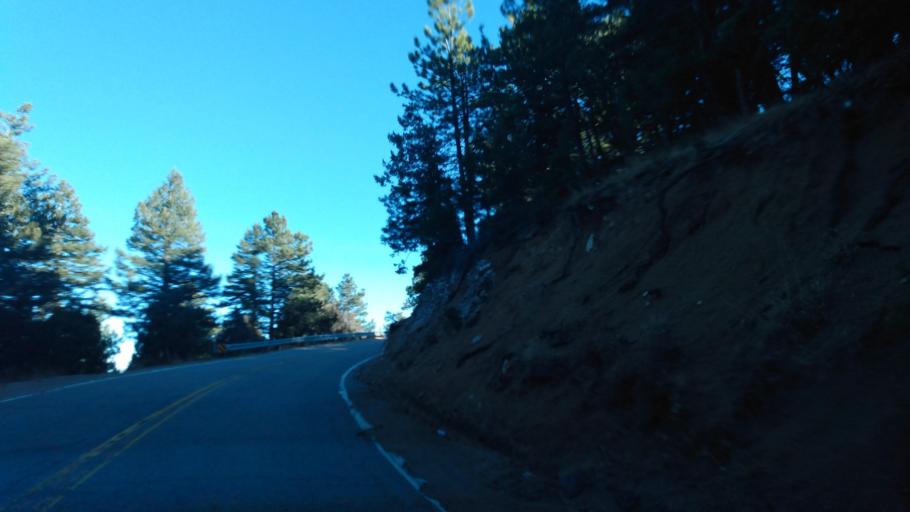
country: US
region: Colorado
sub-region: Boulder County
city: Boulder
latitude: 39.9991
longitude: -105.3554
